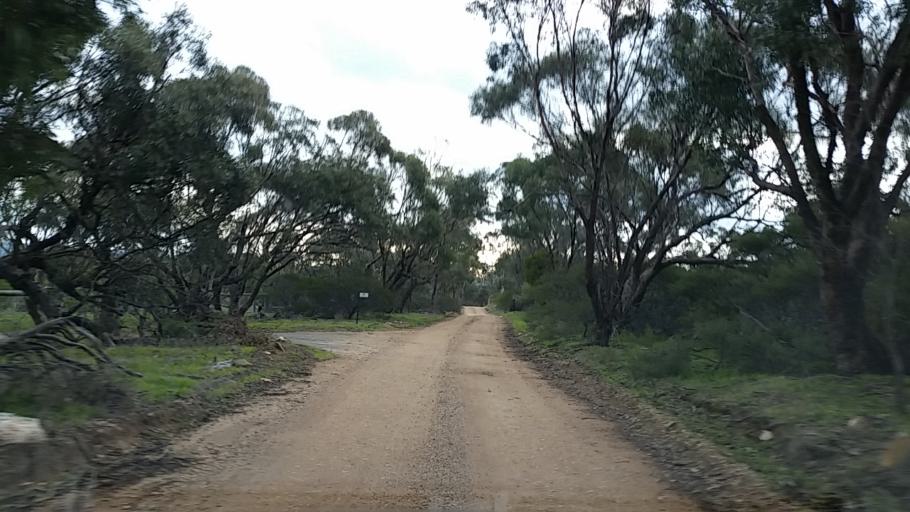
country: AU
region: South Australia
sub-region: Mount Barker
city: Callington
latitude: -34.9996
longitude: 139.0583
